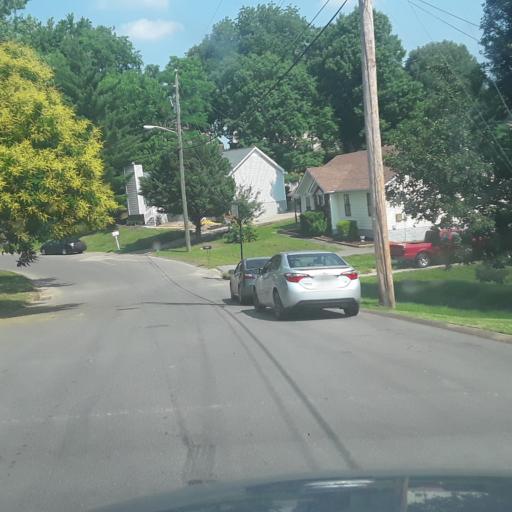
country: US
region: Tennessee
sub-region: Williamson County
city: Brentwood Estates
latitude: 36.0404
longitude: -86.7064
